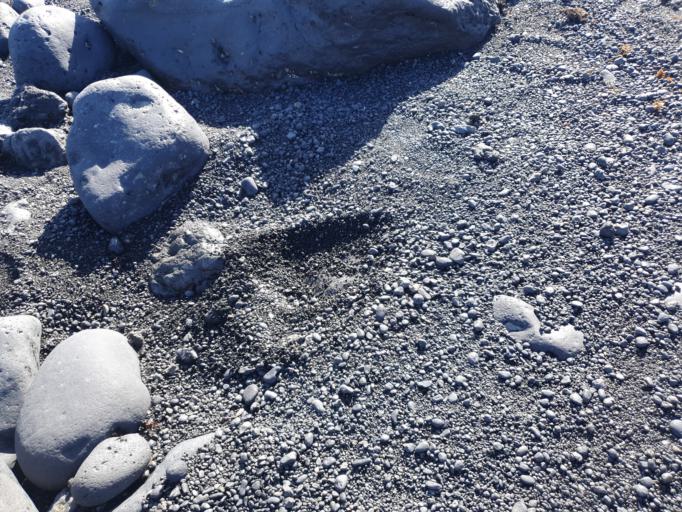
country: ES
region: Canary Islands
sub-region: Provincia de Las Palmas
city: Tinajo
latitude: 29.0640
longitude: -13.7676
